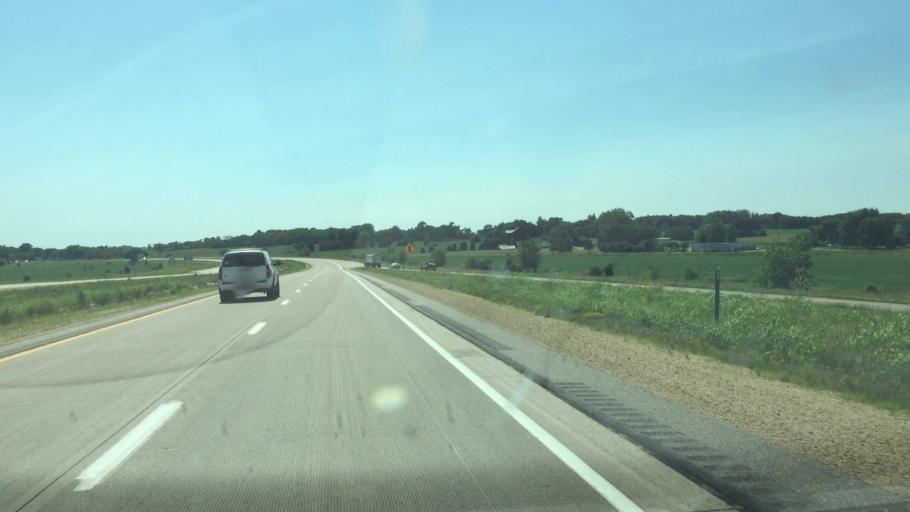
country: US
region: Iowa
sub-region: Jones County
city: Monticello
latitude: 42.2073
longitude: -91.1919
